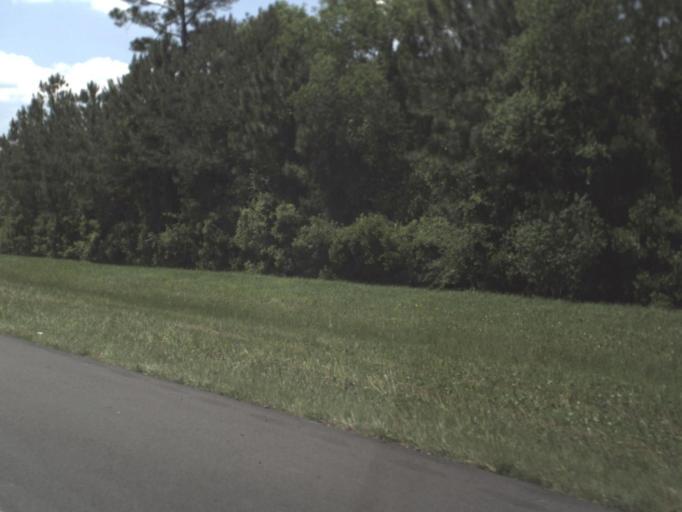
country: US
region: Florida
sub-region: Nassau County
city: Yulee
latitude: 30.6075
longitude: -81.6459
